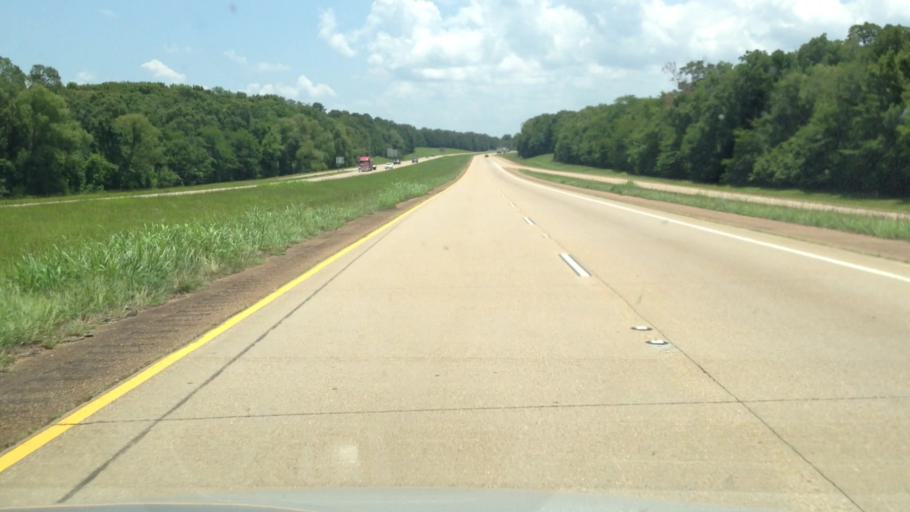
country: US
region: Louisiana
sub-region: Rapides Parish
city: Woodworth
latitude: 31.1615
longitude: -92.4582
